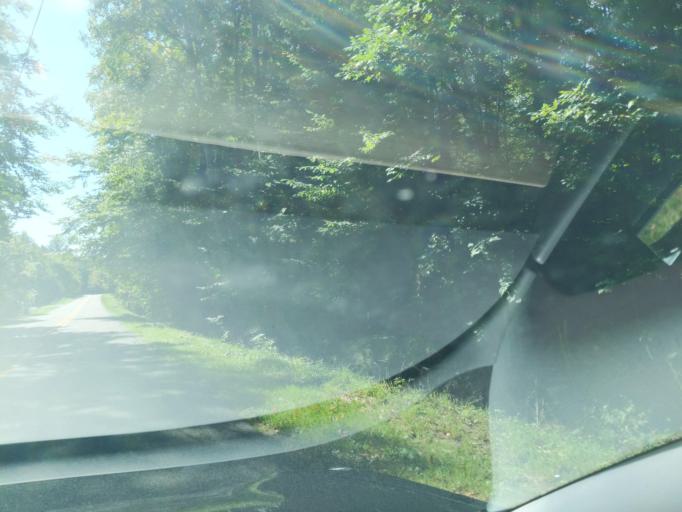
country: US
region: Michigan
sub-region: Antrim County
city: Elk Rapids
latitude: 44.9486
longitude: -85.3233
